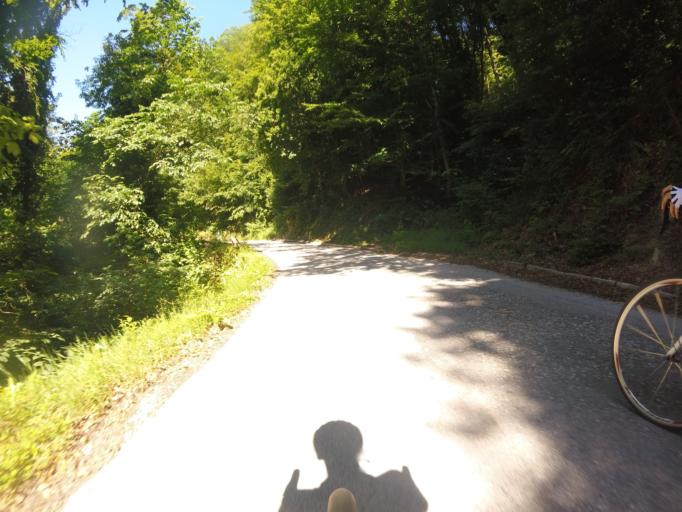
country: SI
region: Brezice
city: Brezice
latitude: 45.8379
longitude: 15.5910
